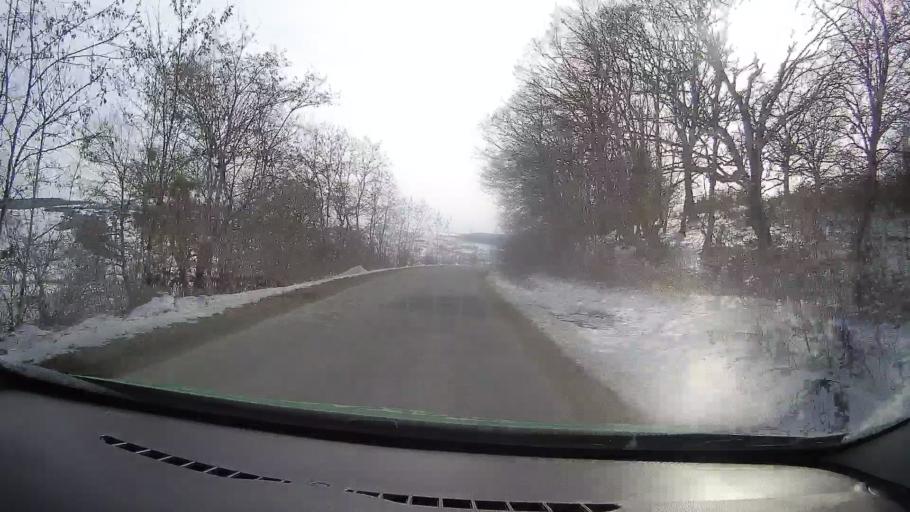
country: RO
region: Sibiu
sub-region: Comuna Bradeni
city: Bradeni
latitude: 46.1024
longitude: 24.8384
